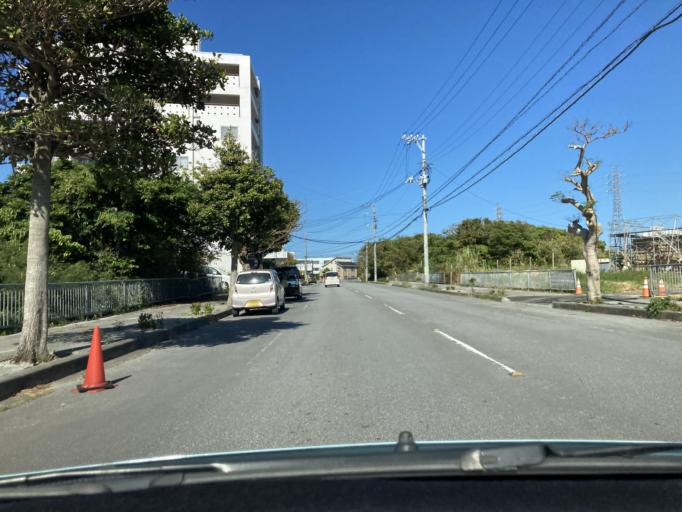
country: JP
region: Okinawa
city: Gushikawa
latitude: 26.3826
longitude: 127.8694
